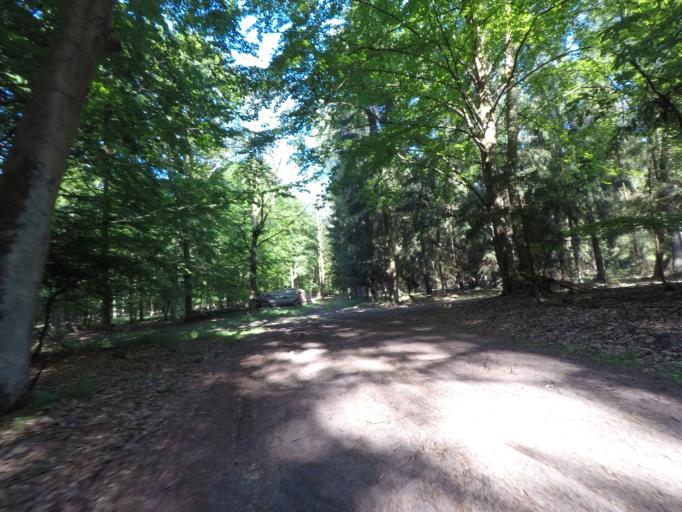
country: DE
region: Brandenburg
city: Marienwerder
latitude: 52.8367
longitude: 13.6349
